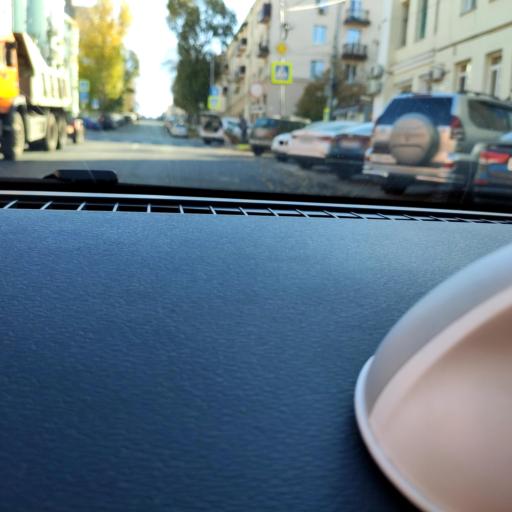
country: RU
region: Samara
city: Rozhdestveno
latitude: 53.1891
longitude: 50.0843
